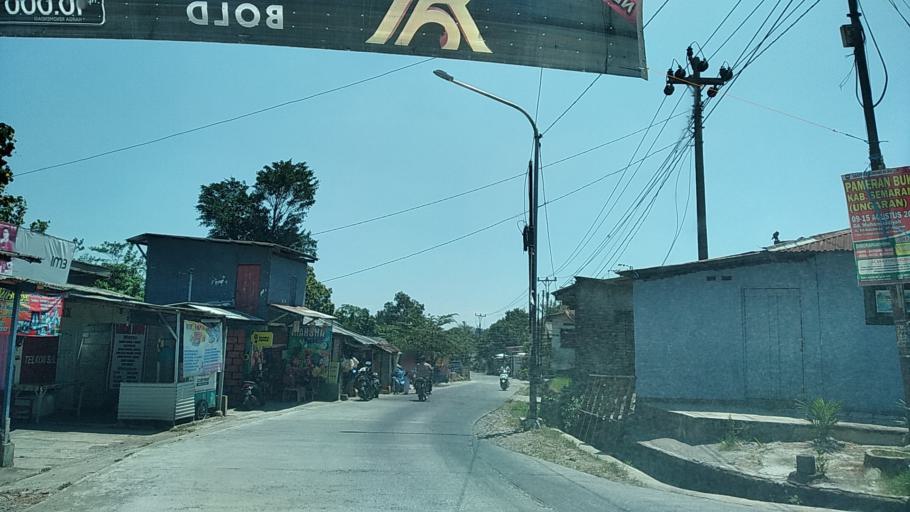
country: ID
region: Central Java
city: Ungaran
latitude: -7.0937
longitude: 110.4106
